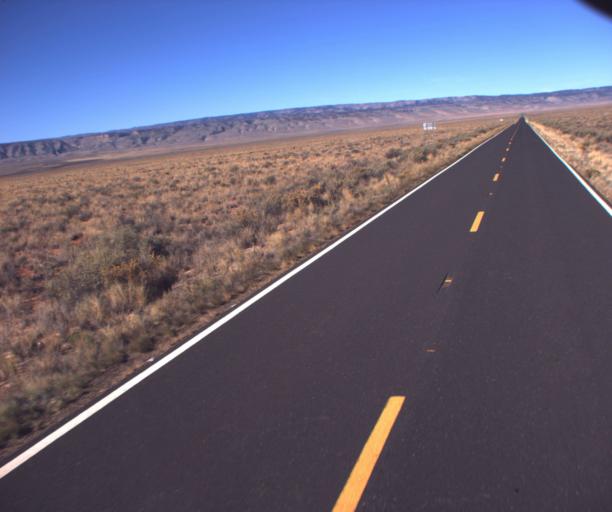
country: US
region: Arizona
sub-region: Coconino County
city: Page
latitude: 36.6966
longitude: -111.9115
